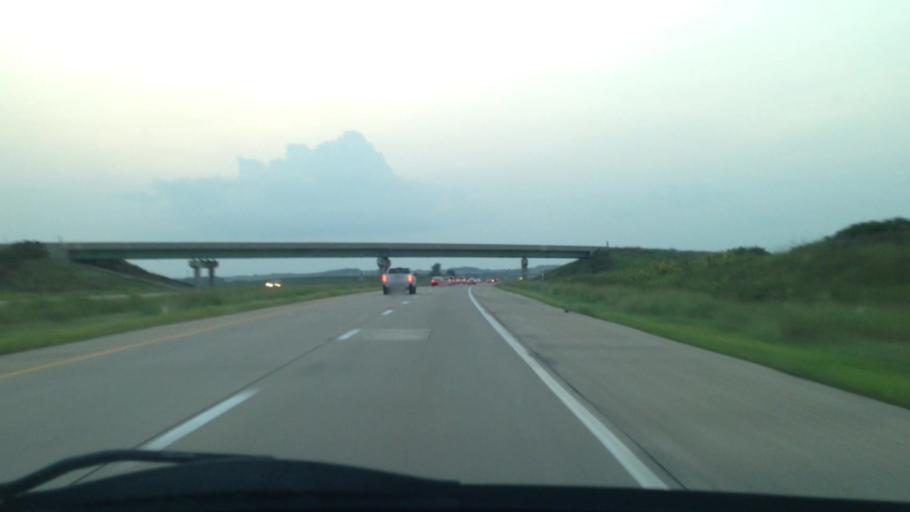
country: US
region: Iowa
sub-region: Black Hawk County
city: La Porte City
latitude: 42.4054
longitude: -92.1600
